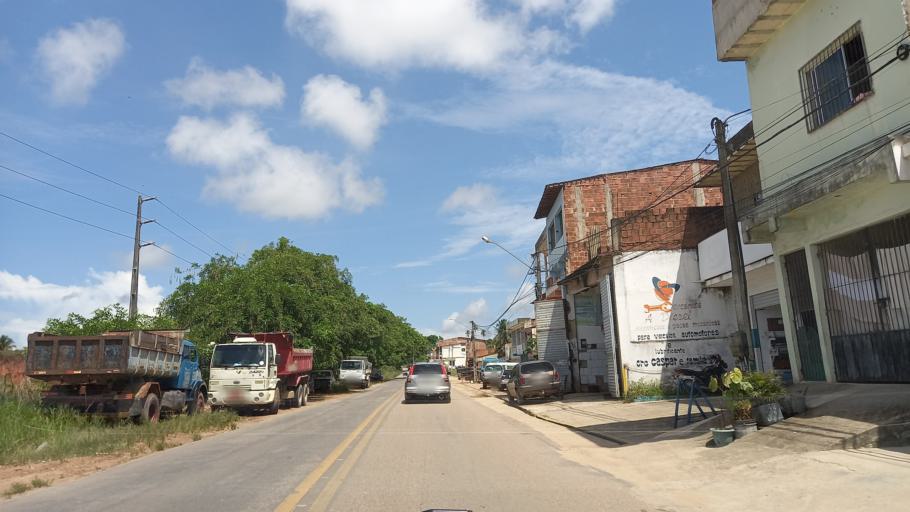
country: BR
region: Pernambuco
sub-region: Barreiros
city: Barreiros
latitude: -8.8157
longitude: -35.1820
